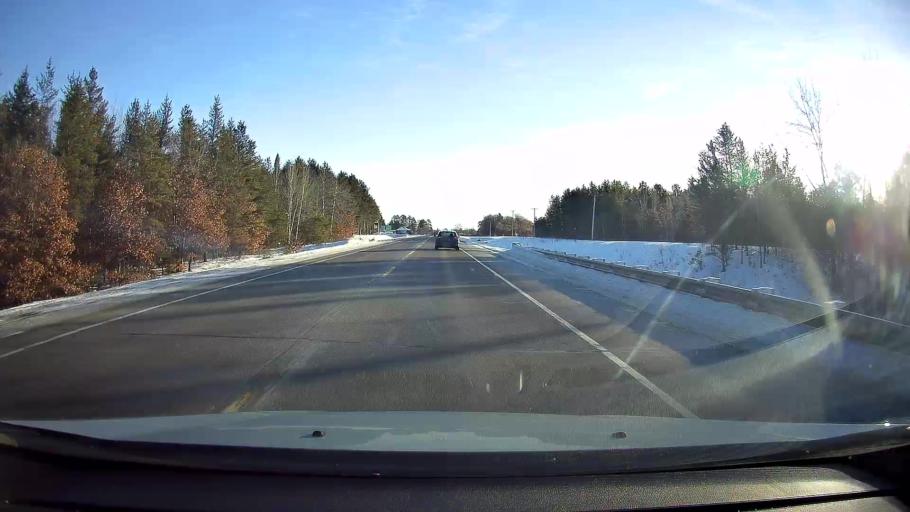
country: US
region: Wisconsin
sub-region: Washburn County
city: Spooner
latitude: 45.9102
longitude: -91.7717
